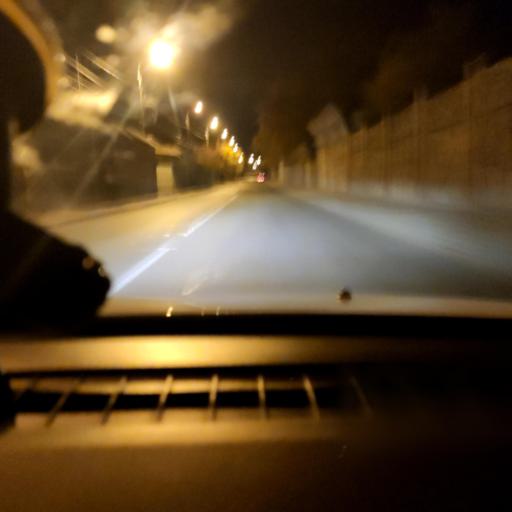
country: RU
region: Samara
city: Samara
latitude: 53.2735
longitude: 50.1919
